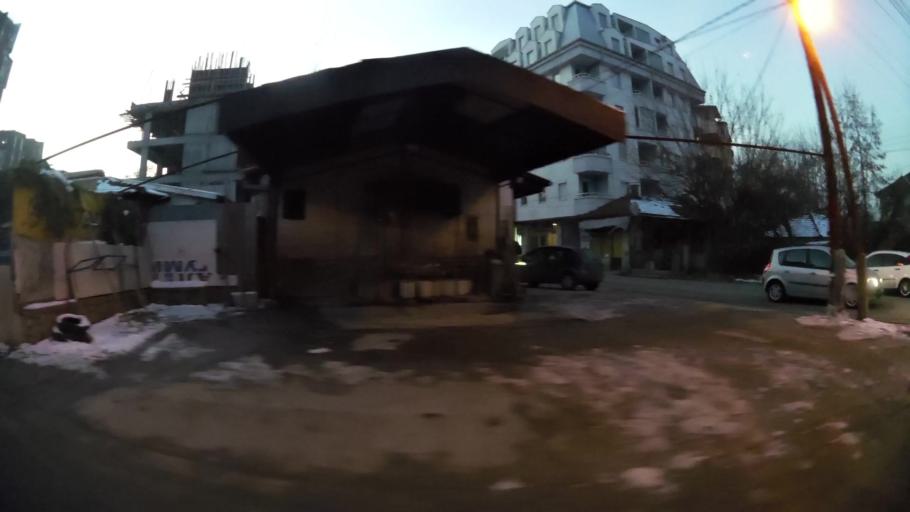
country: MK
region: Karpos
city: Skopje
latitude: 41.9975
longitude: 21.4108
